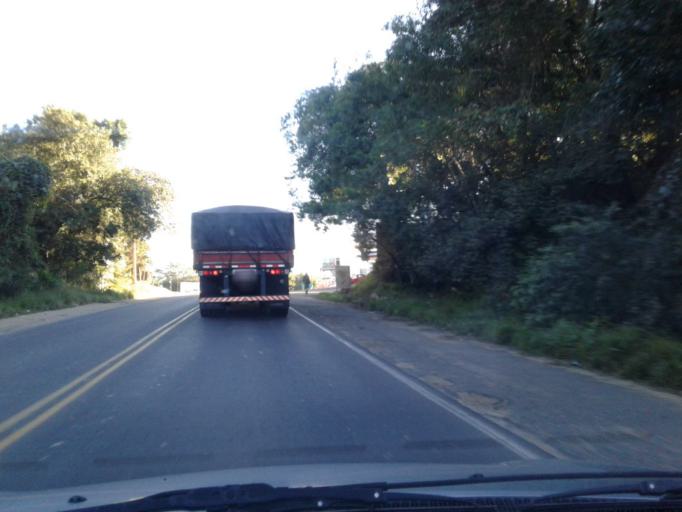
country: BR
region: Rio Grande do Sul
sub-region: Viamao
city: Viamao
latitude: -30.0868
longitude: -51.0221
